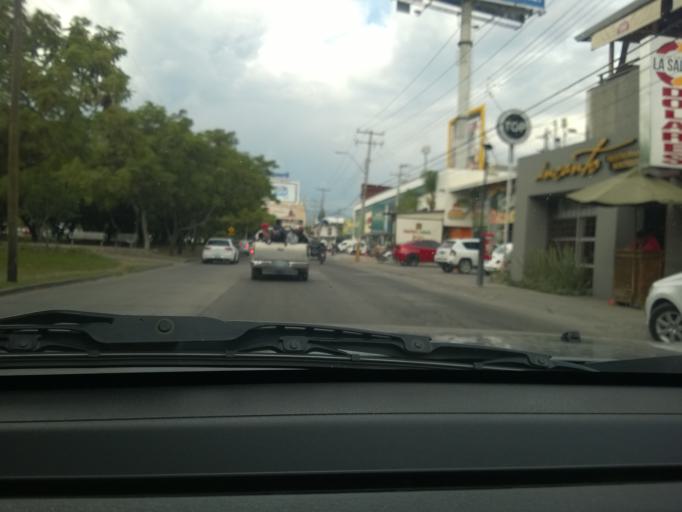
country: MX
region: Guanajuato
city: Leon
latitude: 21.1560
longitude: -101.6936
